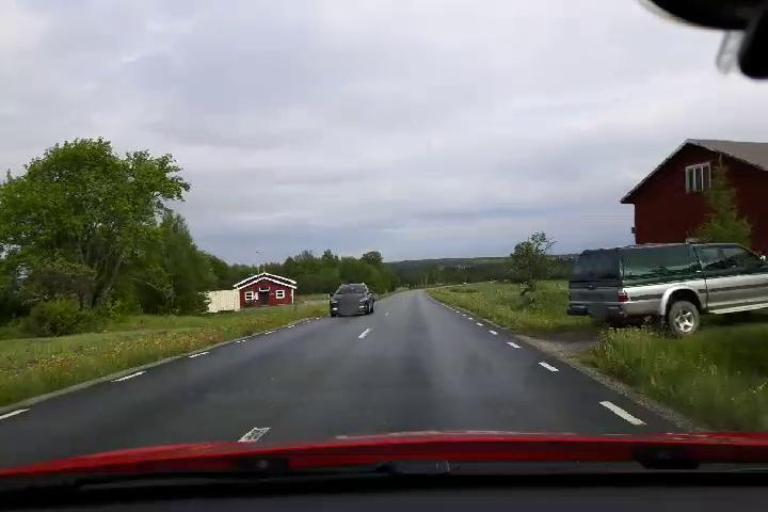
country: SE
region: Jaemtland
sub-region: Bergs Kommun
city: Hoverberg
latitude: 62.9910
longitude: 14.4248
